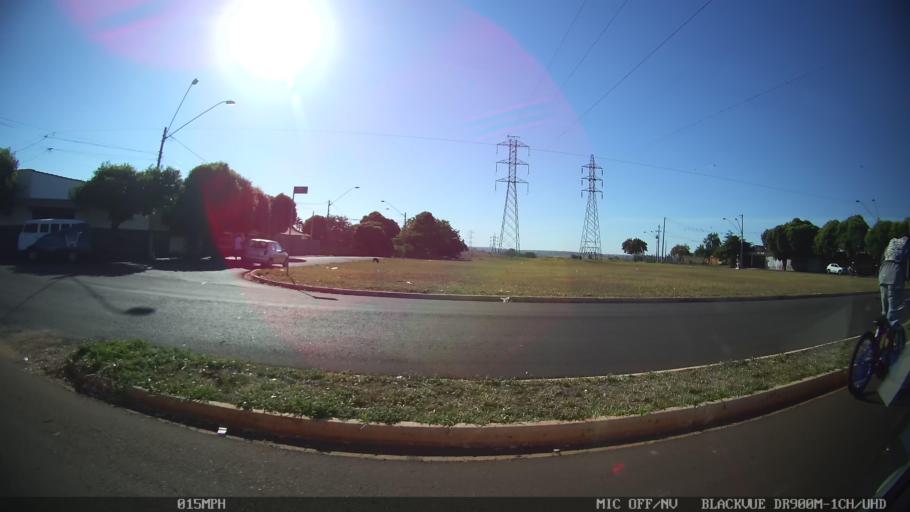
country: BR
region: Sao Paulo
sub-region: Olimpia
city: Olimpia
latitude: -20.7258
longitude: -48.8969
